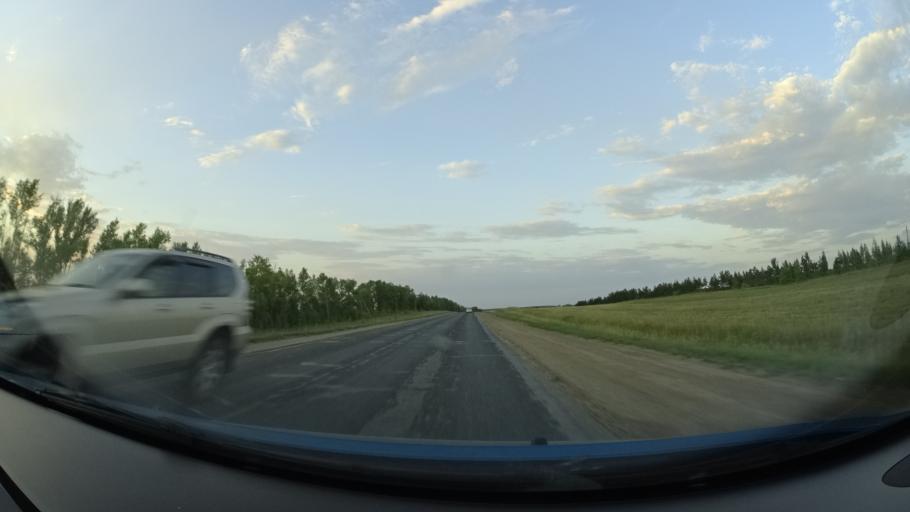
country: RU
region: Orenburg
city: Severnoye
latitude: 54.2083
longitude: 52.7008
